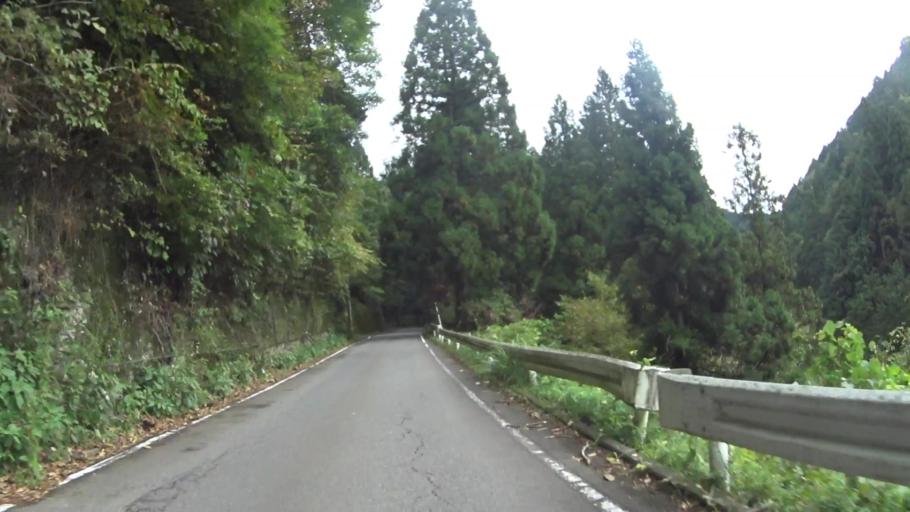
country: JP
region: Shiga Prefecture
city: Kitahama
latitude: 35.2148
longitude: 135.7766
